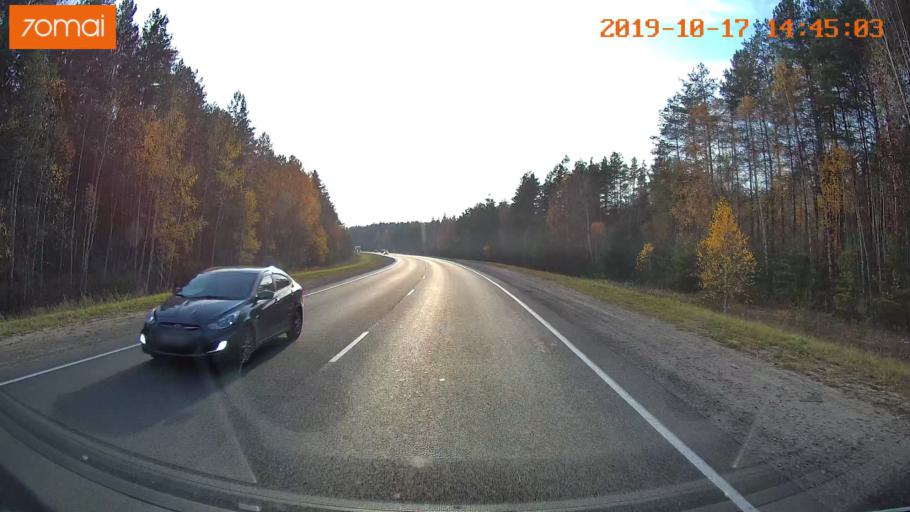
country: RU
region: Rjazan
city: Solotcha
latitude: 54.8051
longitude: 39.8815
